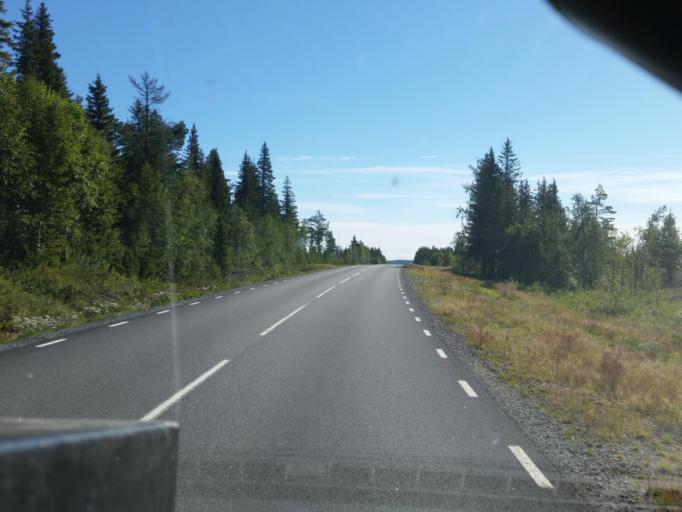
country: SE
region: Vaesterbotten
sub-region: Skelleftea Kommun
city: Storvik
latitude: 65.3267
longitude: 20.7484
